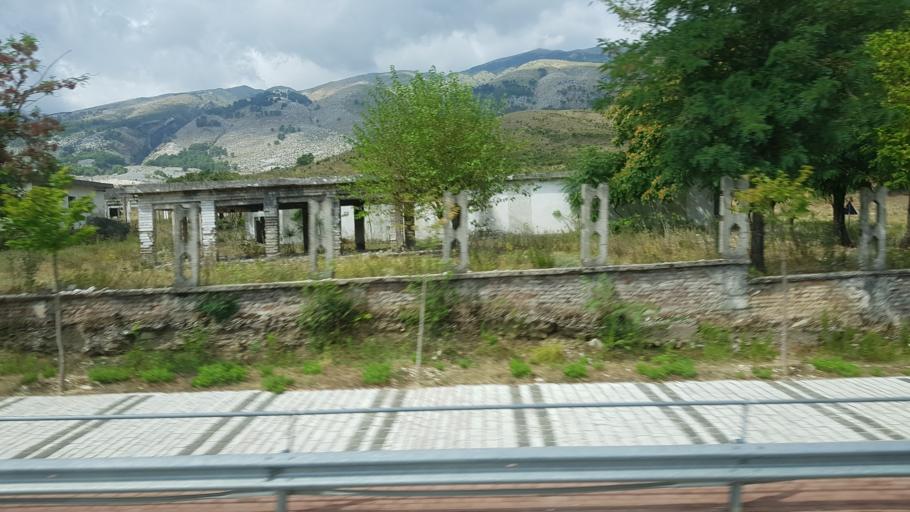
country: AL
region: Gjirokaster
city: Gjirokaster
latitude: 40.0958
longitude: 20.1333
